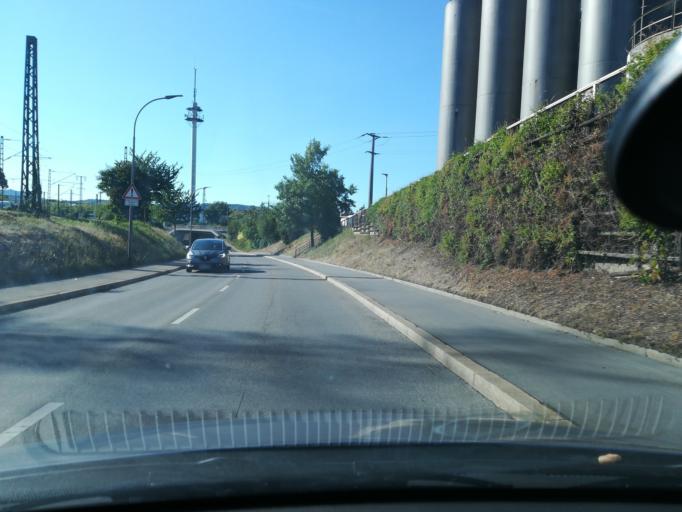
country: DE
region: Baden-Wuerttemberg
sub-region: Freiburg Region
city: Singen
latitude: 47.7599
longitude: 8.8516
